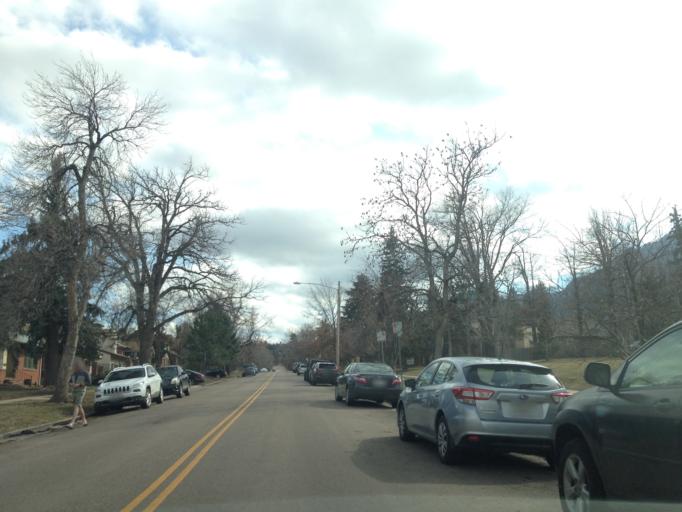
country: US
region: Colorado
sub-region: Boulder County
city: Boulder
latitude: 40.0052
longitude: -105.2762
